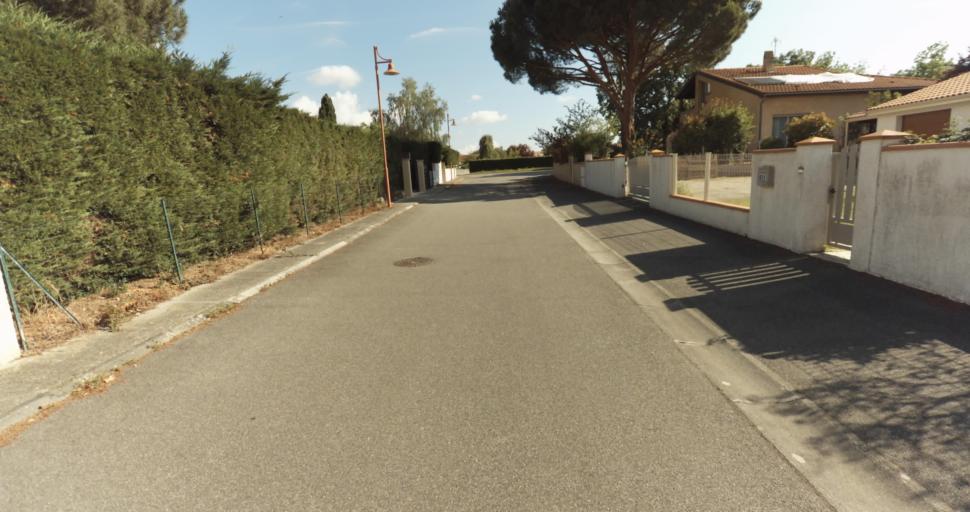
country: FR
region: Midi-Pyrenees
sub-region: Departement de la Haute-Garonne
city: Fontenilles
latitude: 43.5634
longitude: 1.2051
